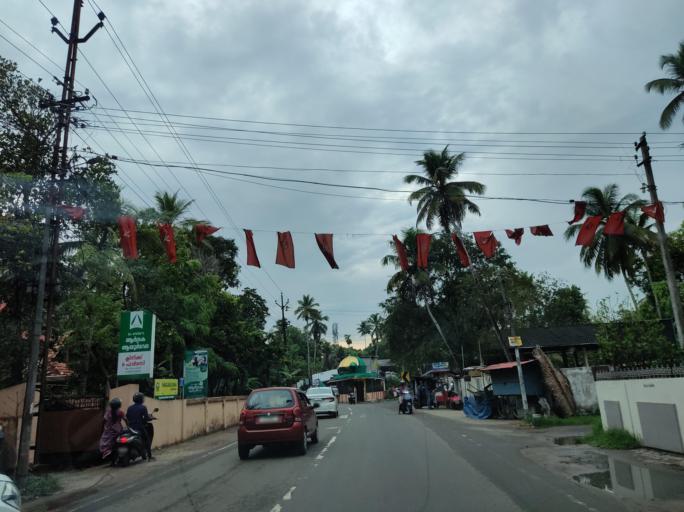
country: IN
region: Kerala
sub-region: Alappuzha
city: Mavelikara
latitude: 9.2509
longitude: 76.4899
